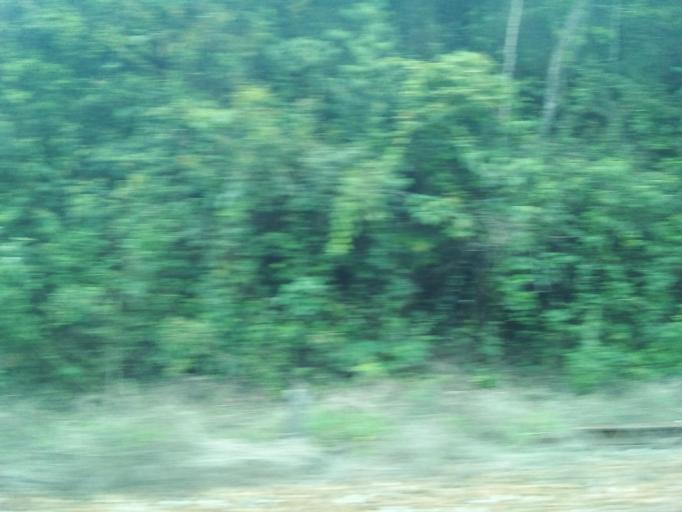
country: BR
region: Minas Gerais
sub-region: Rio Piracicaba
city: Rio Piracicaba
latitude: -19.9711
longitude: -43.2496
